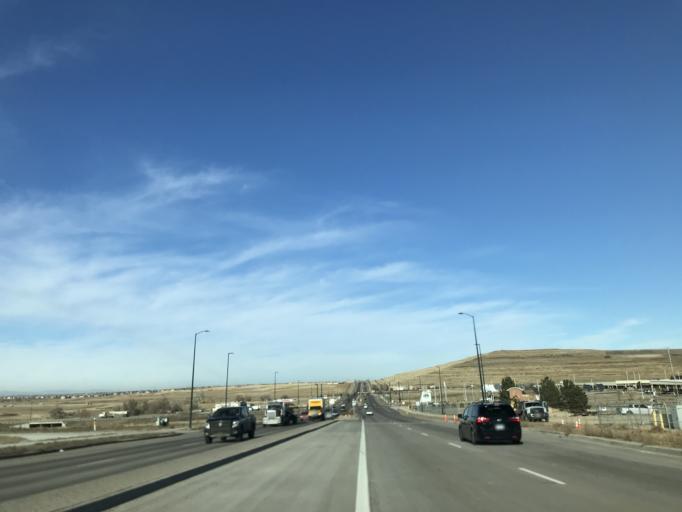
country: US
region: Colorado
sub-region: Adams County
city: Aurora
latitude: 39.8409
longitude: -104.7720
